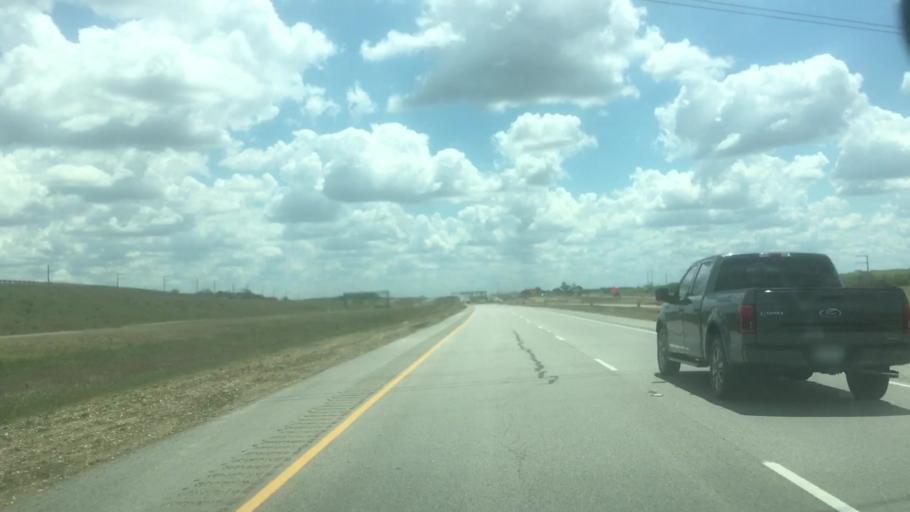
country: US
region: Texas
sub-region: Caldwell County
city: Uhland
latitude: 29.9950
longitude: -97.6856
